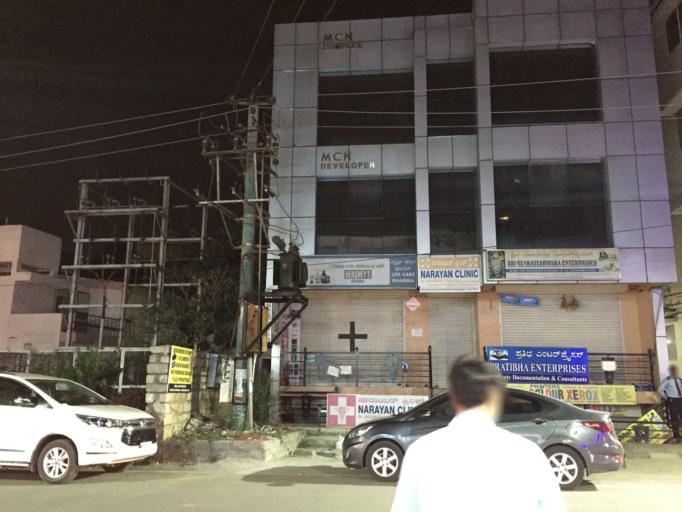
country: IN
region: Karnataka
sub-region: Bangalore Urban
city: Yelahanka
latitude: 13.0580
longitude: 77.5873
